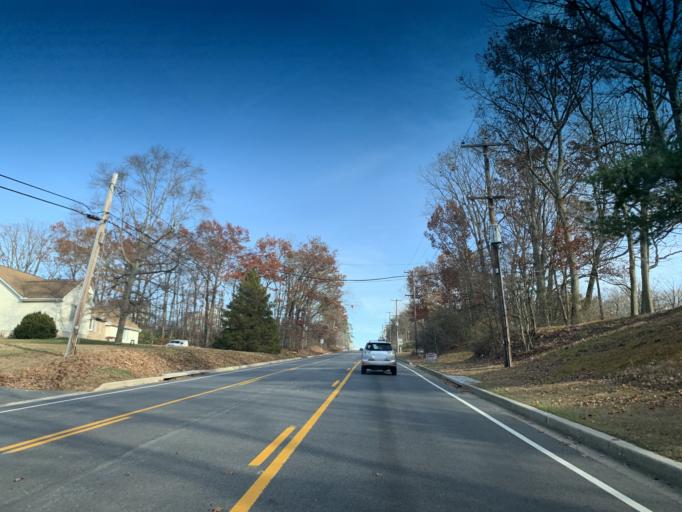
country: US
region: Maryland
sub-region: Cecil County
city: North East
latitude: 39.6025
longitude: -75.9218
